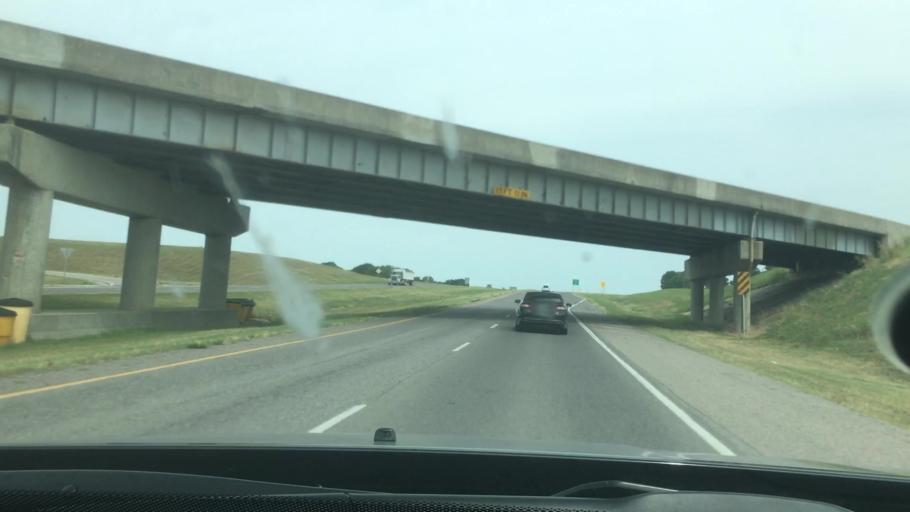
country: US
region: Oklahoma
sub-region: Pontotoc County
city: Ada
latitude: 34.7260
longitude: -96.6344
